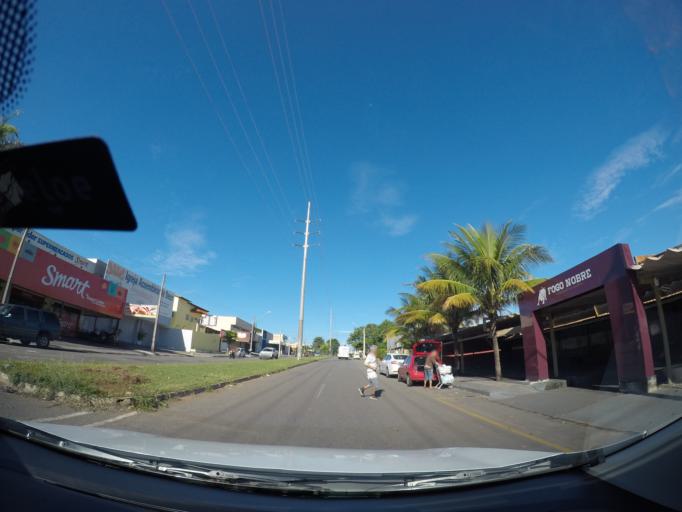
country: BR
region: Goias
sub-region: Goiania
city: Goiania
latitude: -16.7260
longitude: -49.3014
